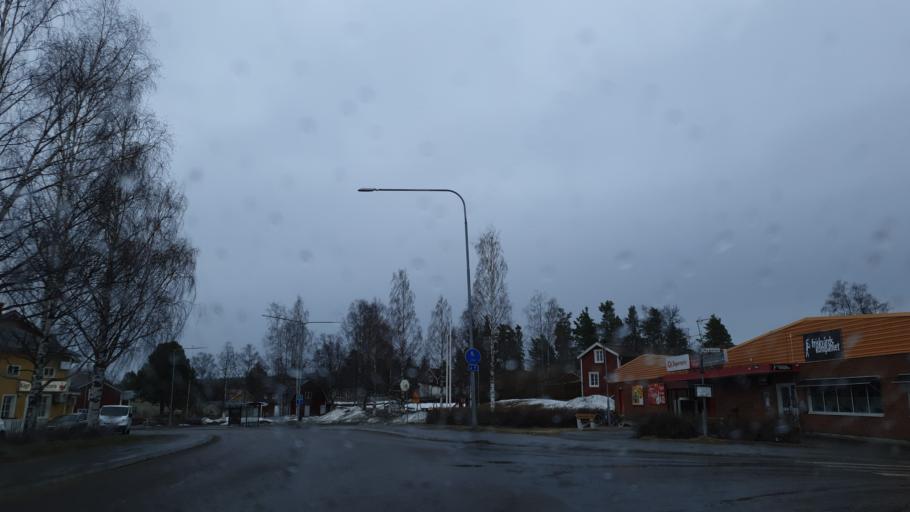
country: SE
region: Vaesterbotten
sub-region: Skelleftea Kommun
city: Kage
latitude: 64.8328
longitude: 20.9885
